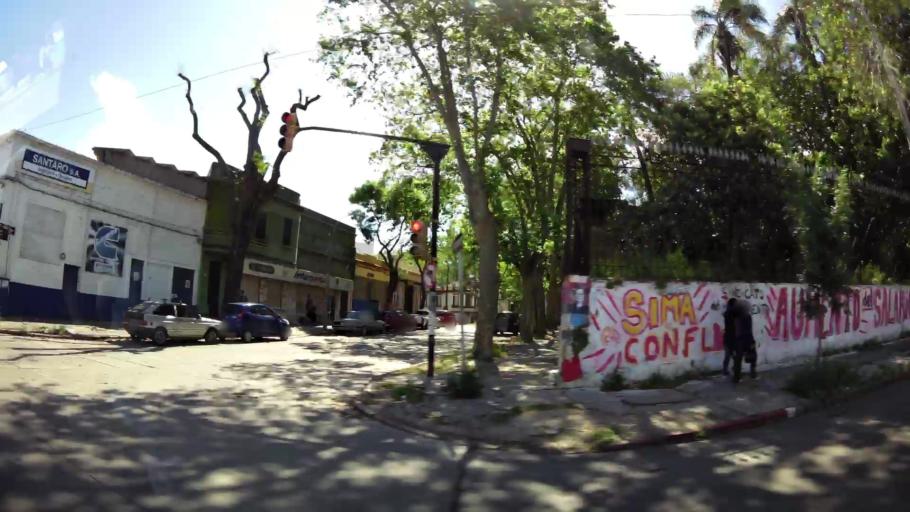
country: UY
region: Montevideo
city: Montevideo
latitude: -34.8805
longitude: -56.1878
